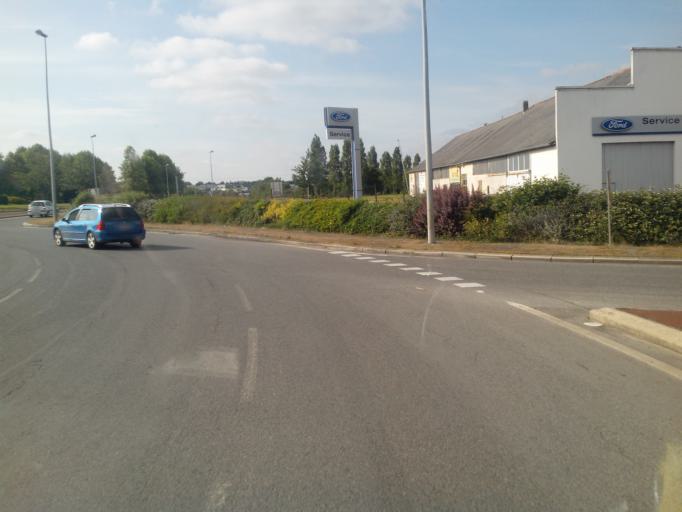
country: FR
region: Brittany
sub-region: Departement d'Ille-et-Vilaine
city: Le Rheu
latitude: 48.0898
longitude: -1.7918
